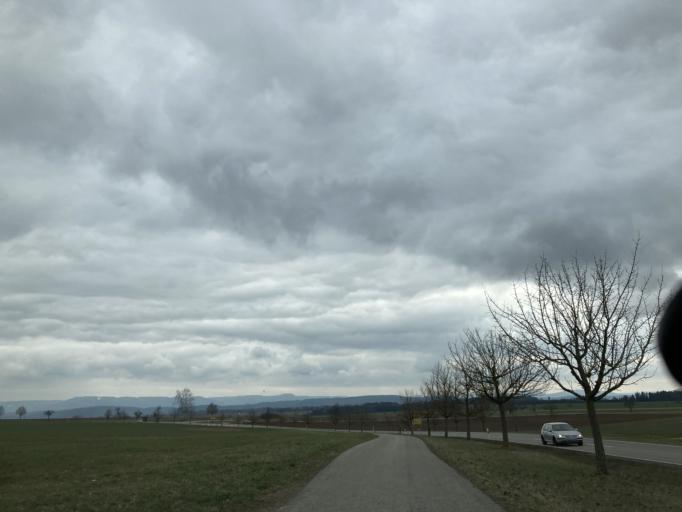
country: DE
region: Baden-Wuerttemberg
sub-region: Tuebingen Region
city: Hirrlingen
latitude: 48.4239
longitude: 8.8287
